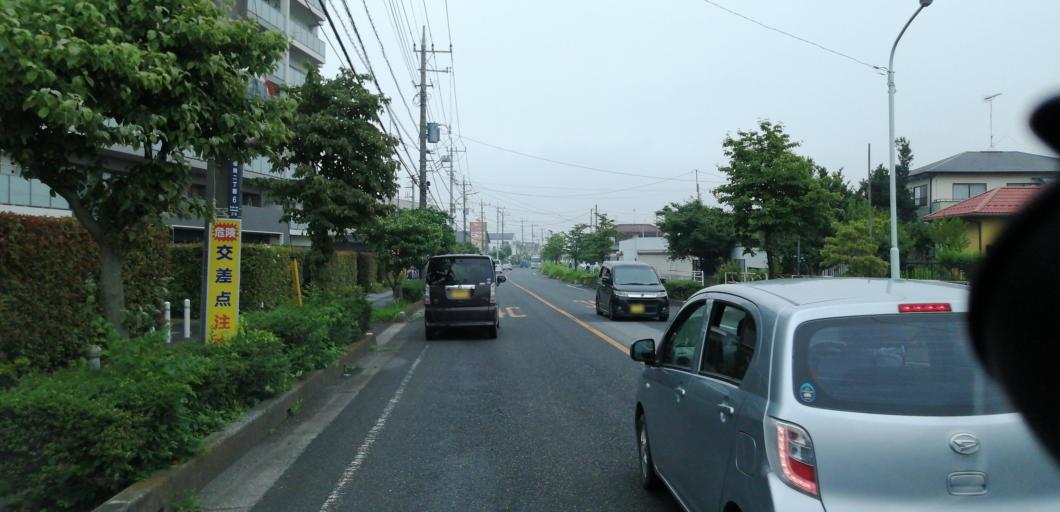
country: JP
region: Saitama
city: Kukichuo
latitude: 36.0953
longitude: 139.6847
